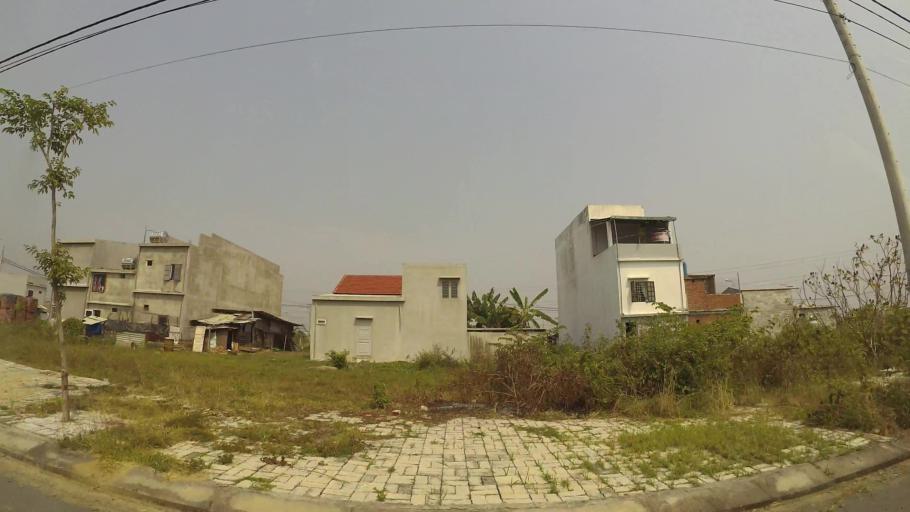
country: VN
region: Da Nang
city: Cam Le
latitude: 15.9687
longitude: 108.2142
